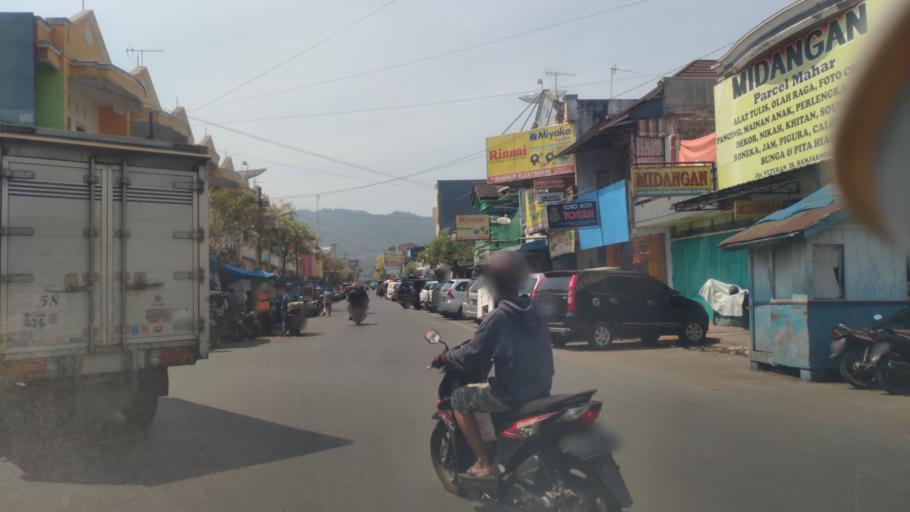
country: ID
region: Central Java
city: Wonosobo
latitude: -7.3931
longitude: 109.7006
